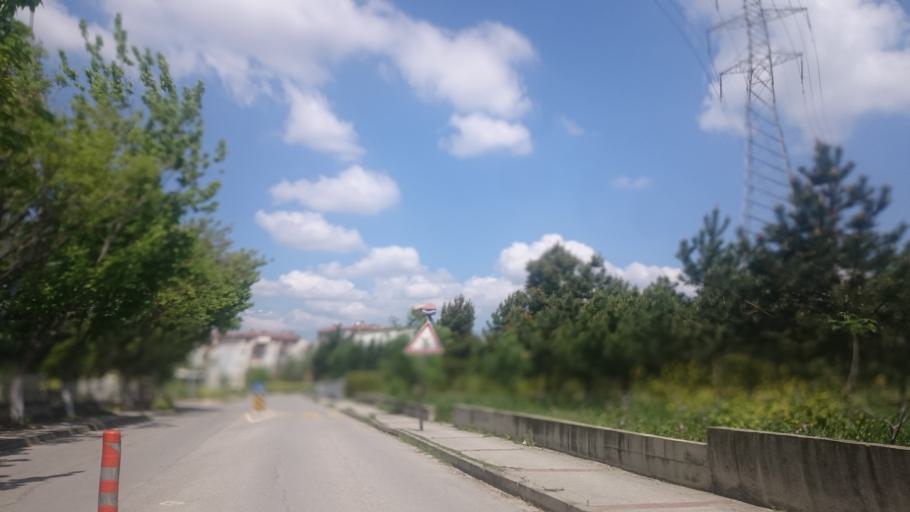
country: TR
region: Bursa
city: Niluefer
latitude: 40.2239
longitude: 28.9657
